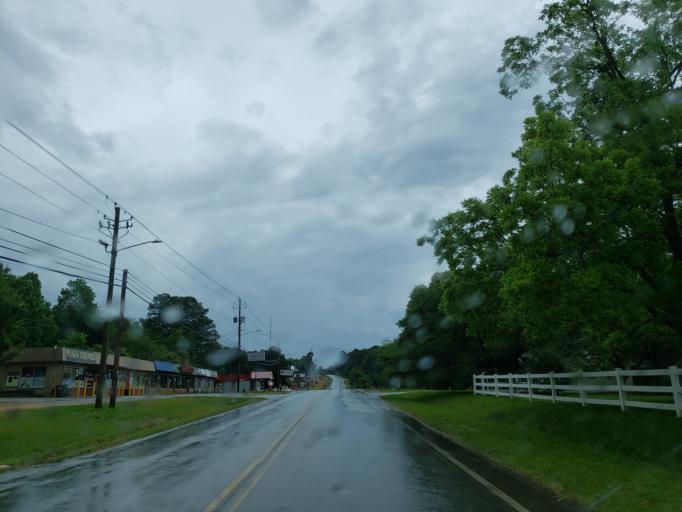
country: US
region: Georgia
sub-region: Haralson County
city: Buchanan
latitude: 33.7971
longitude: -85.1881
